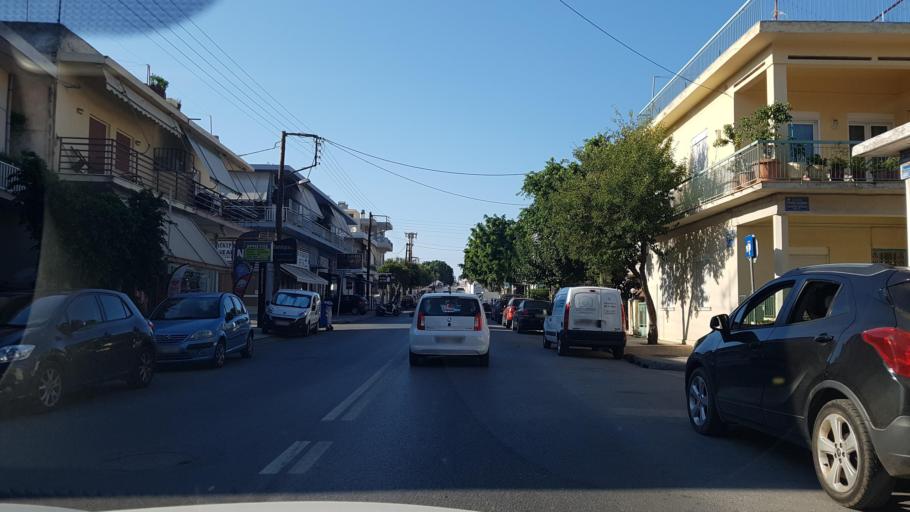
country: GR
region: Crete
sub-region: Nomos Chanias
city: Chania
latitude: 35.5047
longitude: 24.0197
